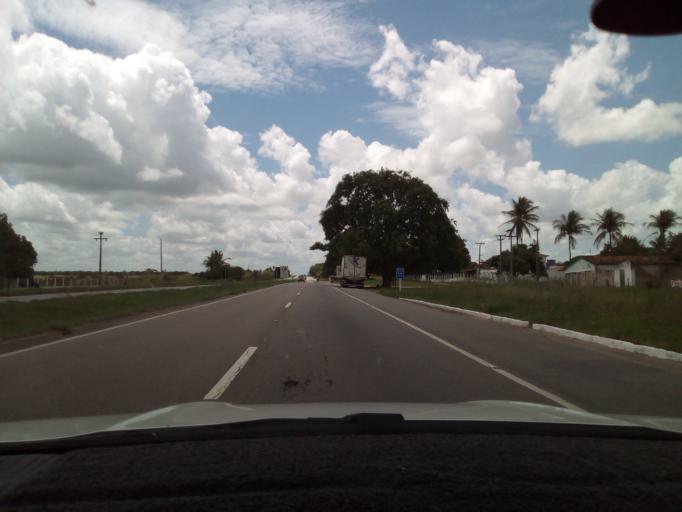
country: BR
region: Paraiba
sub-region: Pilar
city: Pilar
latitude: -7.1851
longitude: -35.2952
